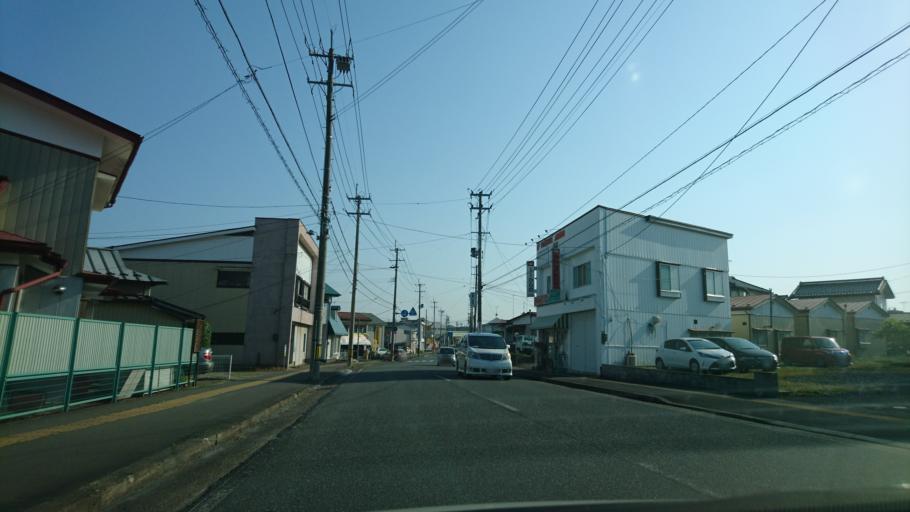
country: JP
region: Iwate
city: Ichinoseki
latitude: 38.9331
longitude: 141.1244
